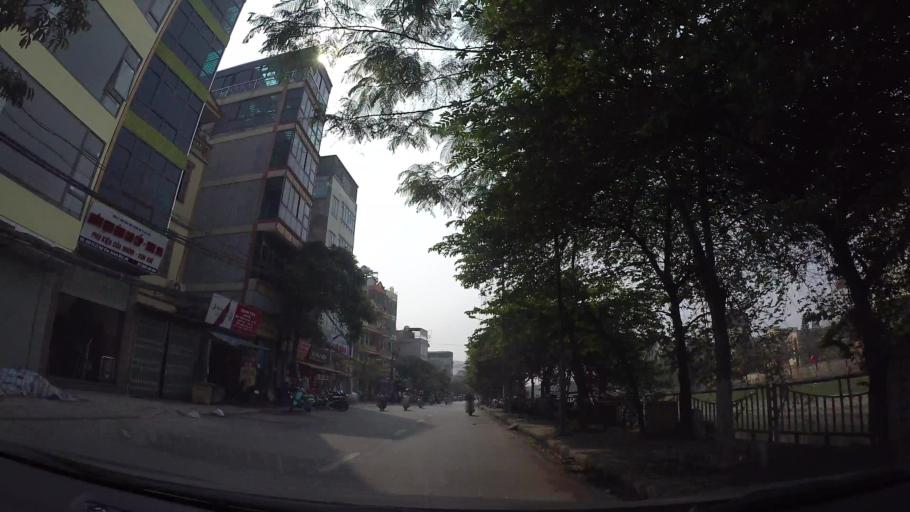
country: VN
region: Ha Noi
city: Thanh Xuan
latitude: 20.9790
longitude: 105.8214
